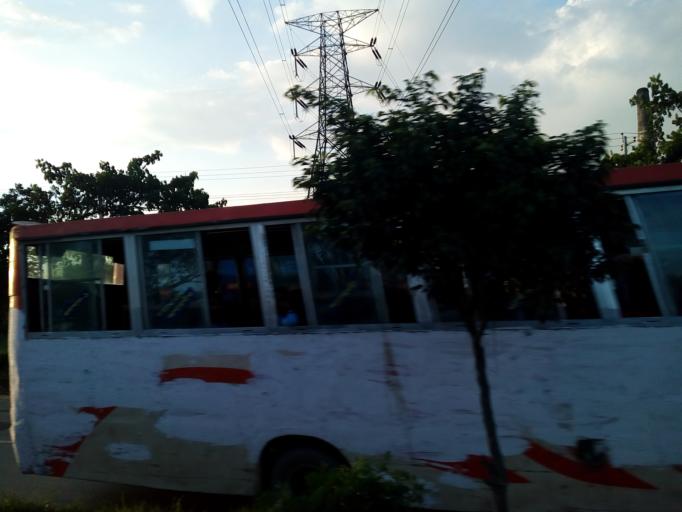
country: BD
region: Dhaka
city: Azimpur
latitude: 23.7903
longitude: 90.3142
